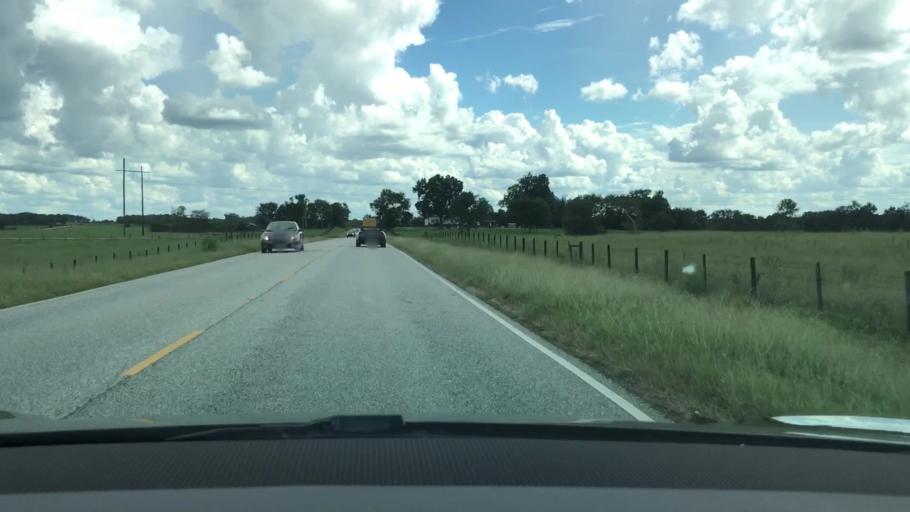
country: US
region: Alabama
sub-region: Montgomery County
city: Pike Road
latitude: 32.2635
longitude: -86.0991
